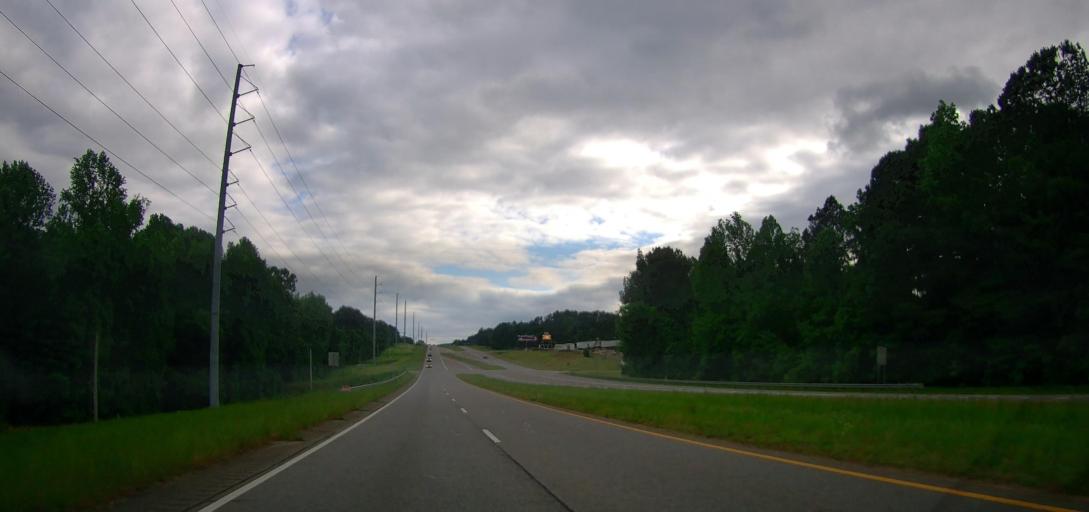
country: US
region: Georgia
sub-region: Oconee County
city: Bogart
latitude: 33.9321
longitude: -83.5078
